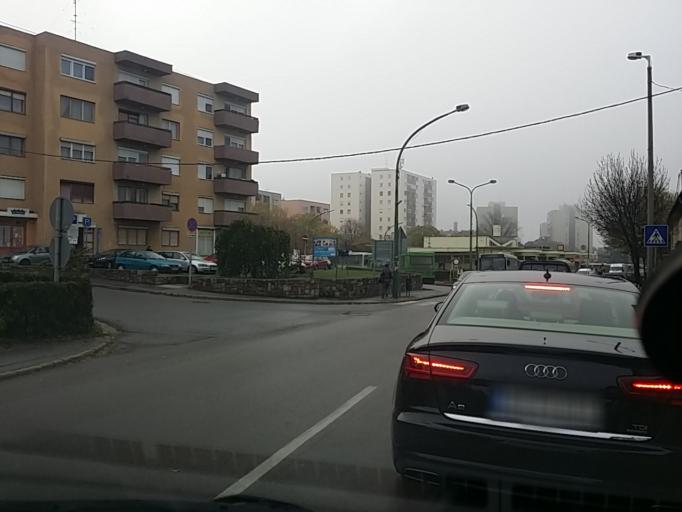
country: HU
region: Heves
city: Gyongyos
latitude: 47.7838
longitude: 19.9306
